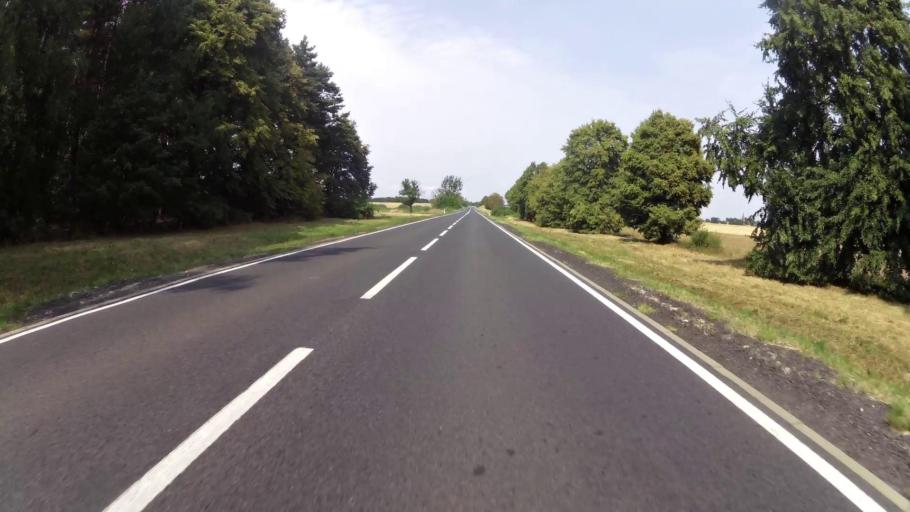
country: PL
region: West Pomeranian Voivodeship
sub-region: Powiat gryfinski
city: Mieszkowice
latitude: 52.8370
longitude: 14.4936
